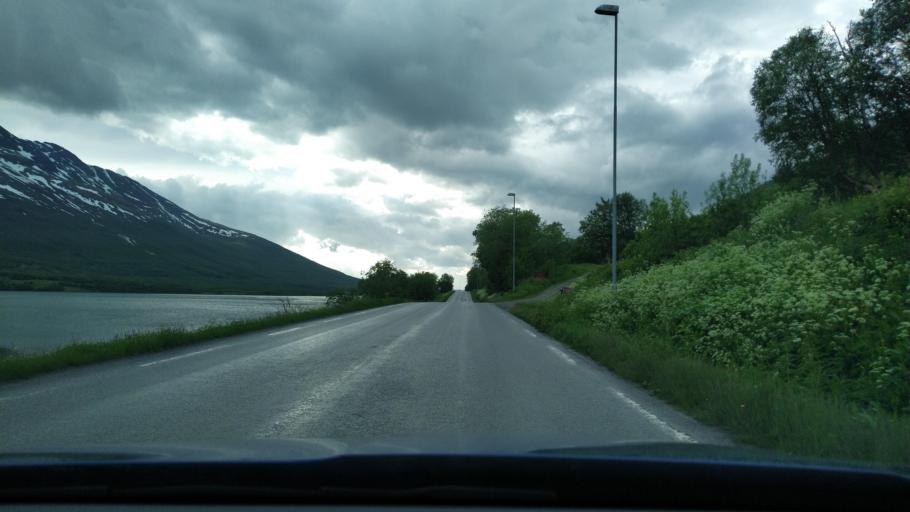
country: NO
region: Troms
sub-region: Balsfjord
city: Storsteinnes
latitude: 69.2205
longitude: 19.5342
